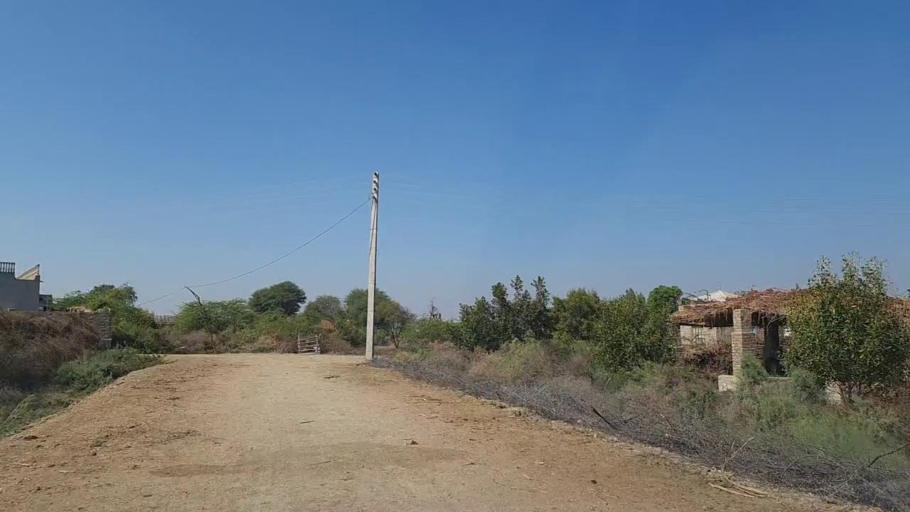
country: PK
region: Sindh
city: Pithoro
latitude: 25.4316
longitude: 69.3733
